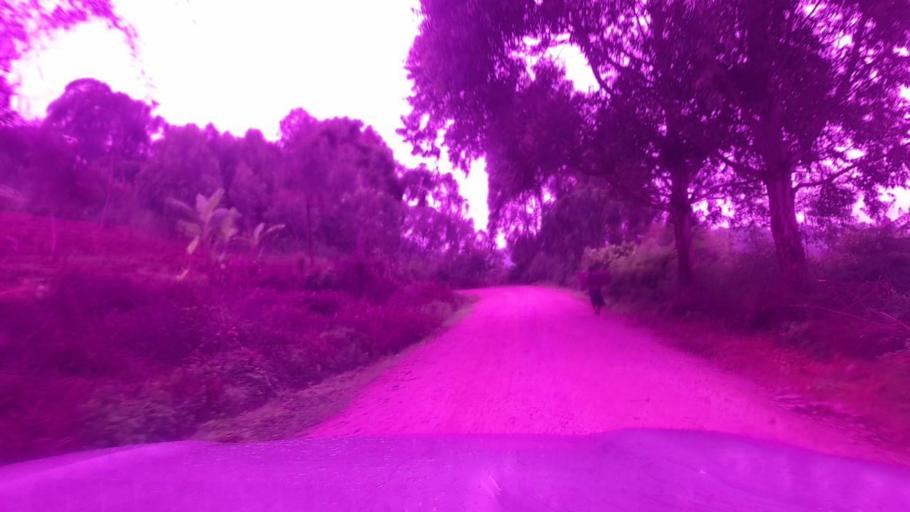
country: ET
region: Southern Nations, Nationalities, and People's Region
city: Bonga
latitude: 7.4678
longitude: 36.1228
